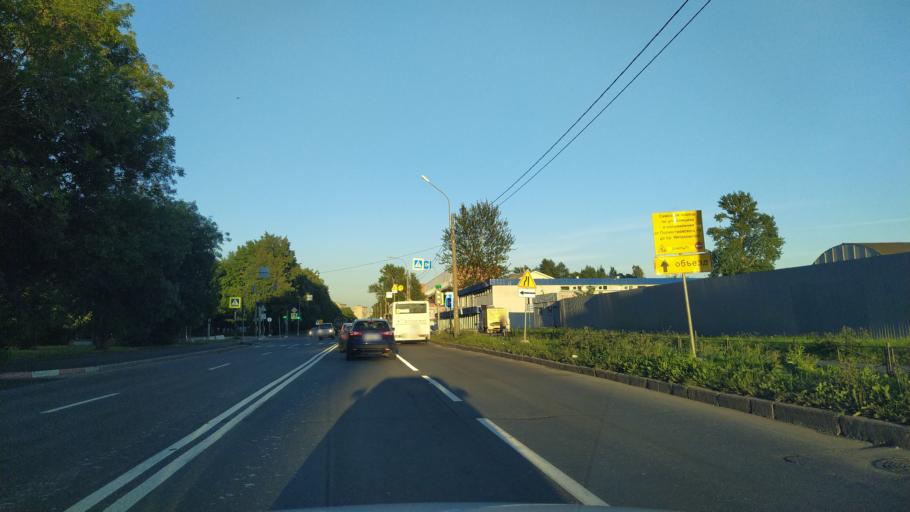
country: RU
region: Leningrad
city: Finlyandskiy
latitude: 59.9676
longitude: 30.3920
